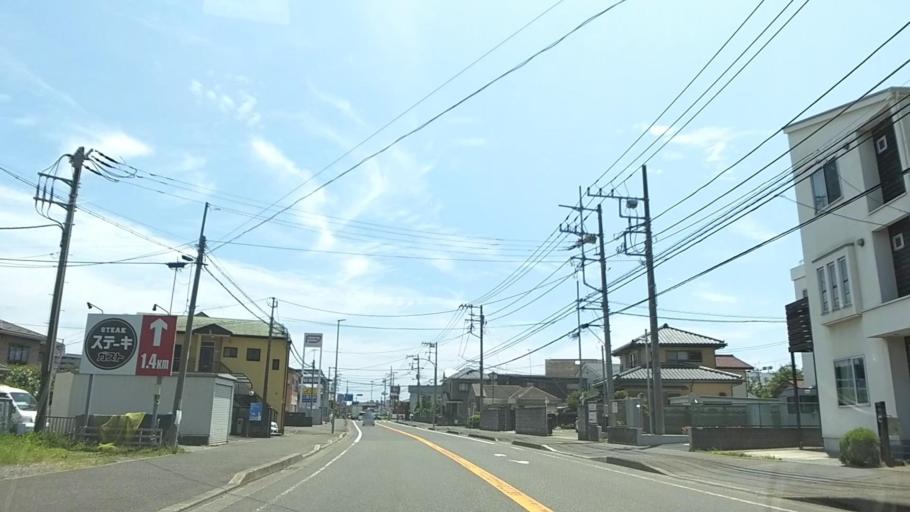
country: JP
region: Kanagawa
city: Atsugi
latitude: 35.3872
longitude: 139.3811
